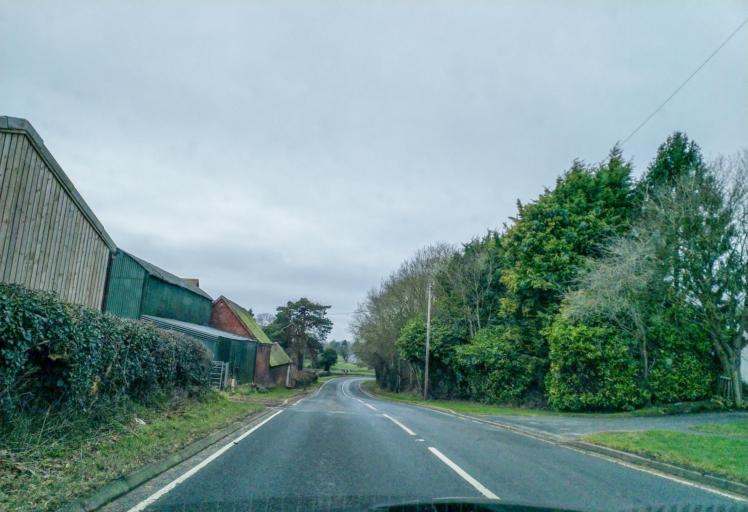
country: GB
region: England
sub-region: Warwickshire
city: Wroxall
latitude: 52.3018
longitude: -1.6631
